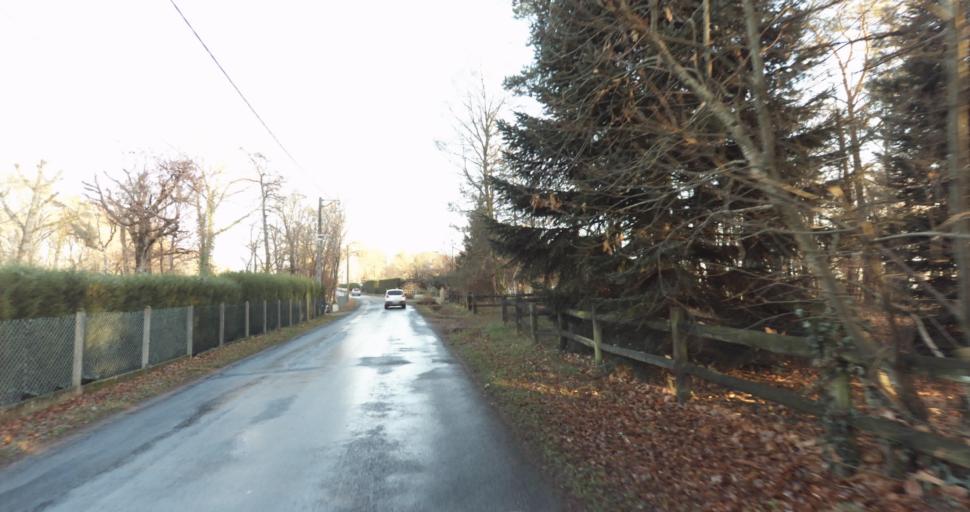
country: FR
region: Limousin
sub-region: Departement de la Haute-Vienne
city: Aixe-sur-Vienne
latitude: 45.8152
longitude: 1.1575
